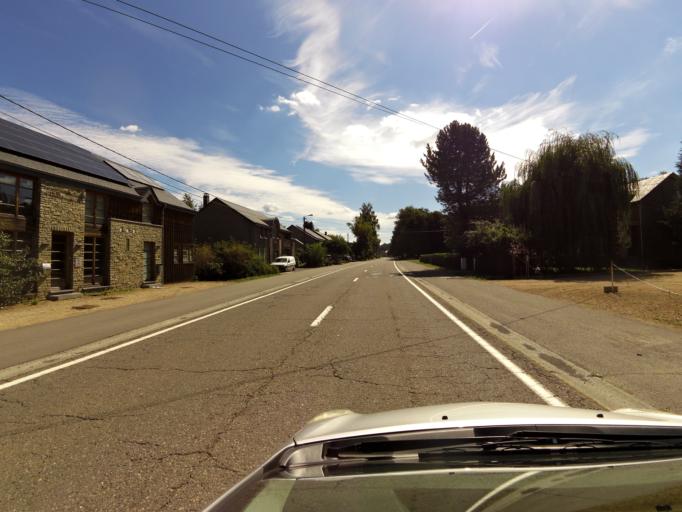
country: BE
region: Wallonia
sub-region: Province du Luxembourg
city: Rendeux
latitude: 50.2393
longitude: 5.5036
